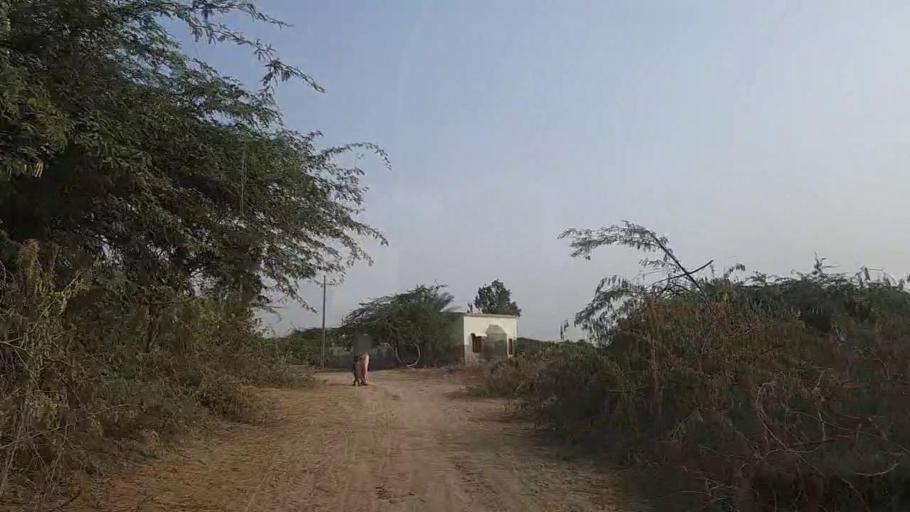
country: PK
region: Sindh
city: Gharo
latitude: 24.6537
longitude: 67.6187
